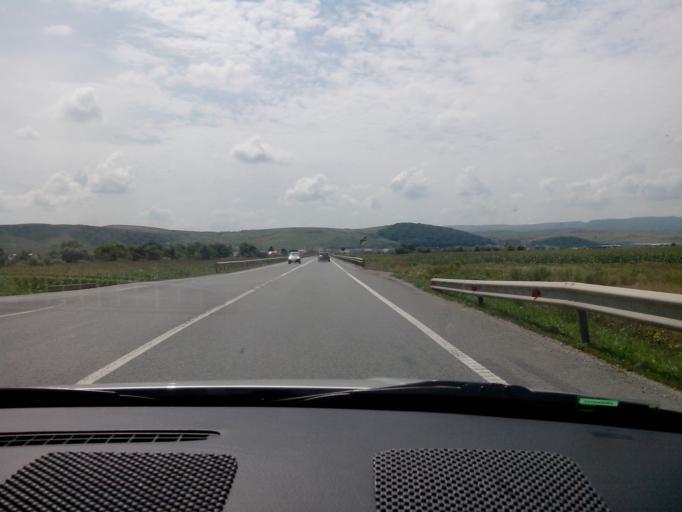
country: RO
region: Cluj
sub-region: Comuna Apahida
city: Sannicoara
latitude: 46.7951
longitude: 23.7179
